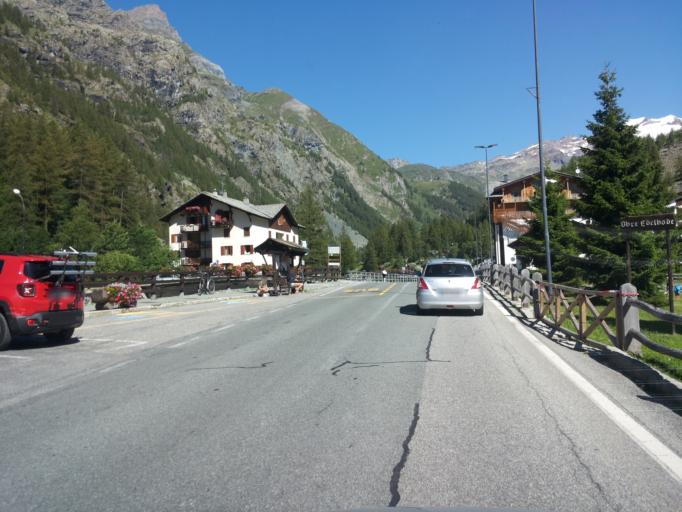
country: IT
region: Aosta Valley
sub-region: Valle d'Aosta
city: Gressoney-La-Trinite
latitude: 45.8316
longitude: 7.8226
